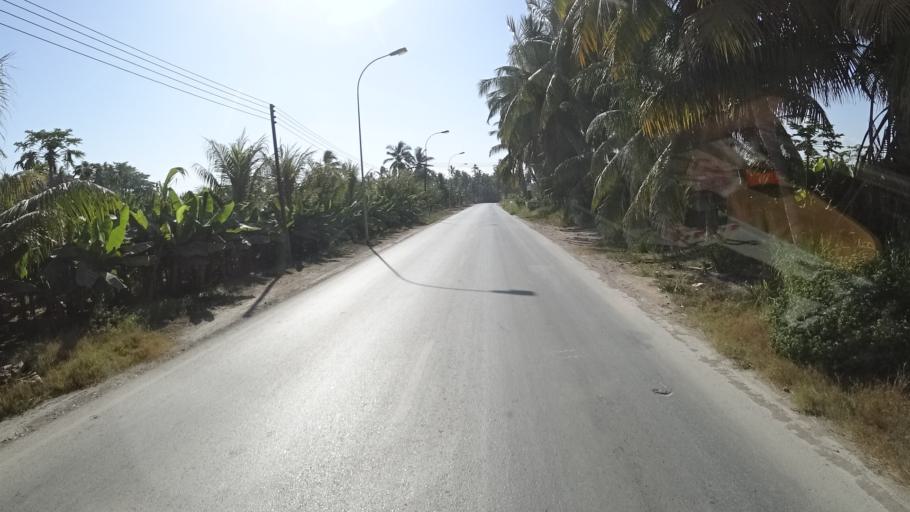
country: OM
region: Zufar
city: Salalah
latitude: 17.0125
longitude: 54.1163
